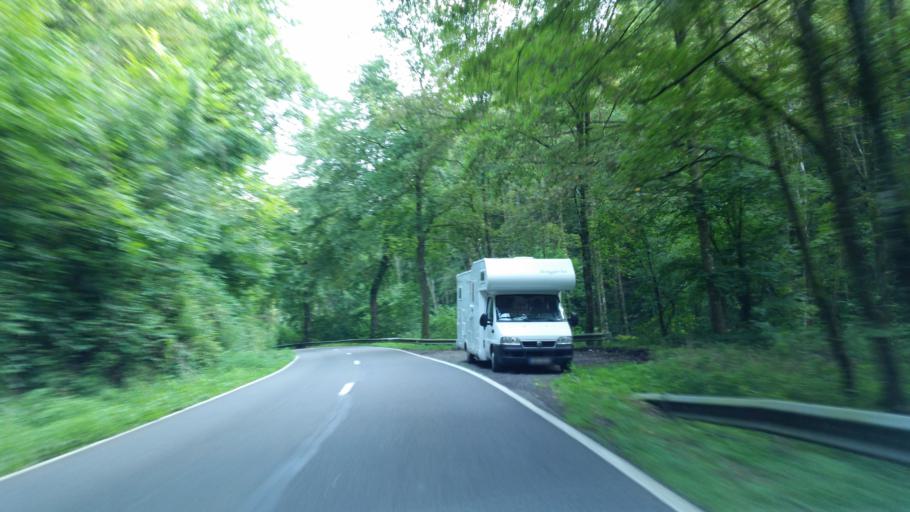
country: BE
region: Wallonia
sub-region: Province du Luxembourg
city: Durbuy
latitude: 50.3606
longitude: 5.4557
